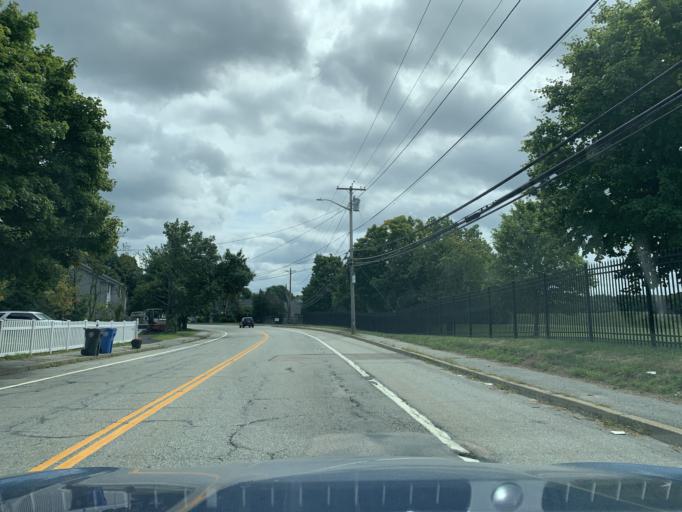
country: US
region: Rhode Island
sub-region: Providence County
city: Johnston
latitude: 41.7796
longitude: -71.4910
